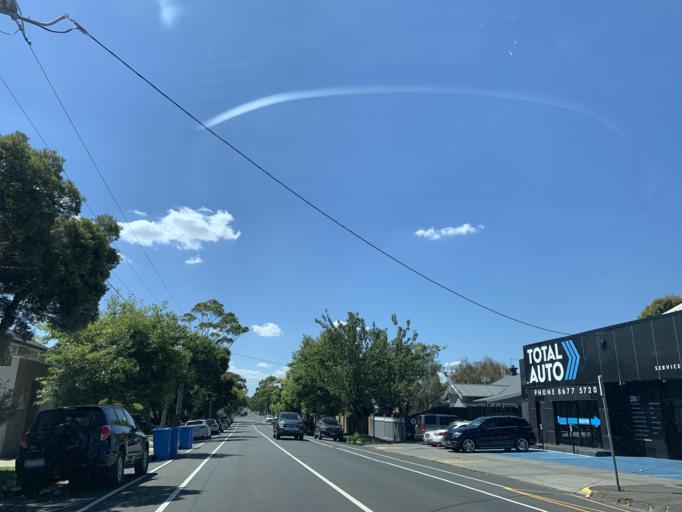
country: AU
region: Victoria
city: Ripponlea
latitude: -37.8941
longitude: 144.9951
